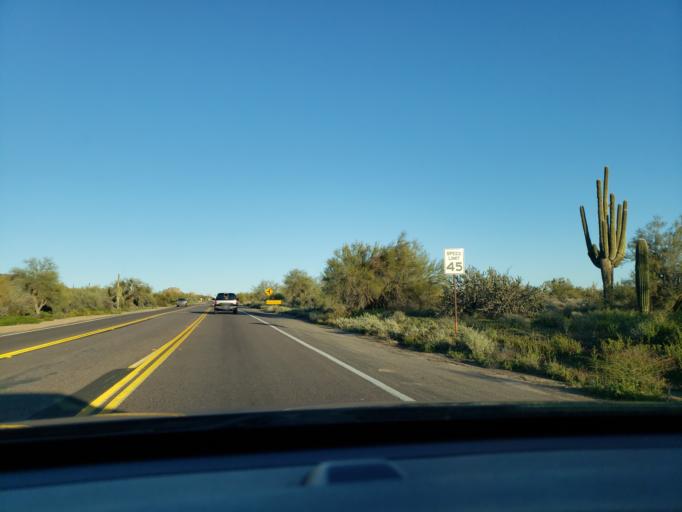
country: US
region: Arizona
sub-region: Maricopa County
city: Cave Creek
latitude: 33.7991
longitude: -111.9592
